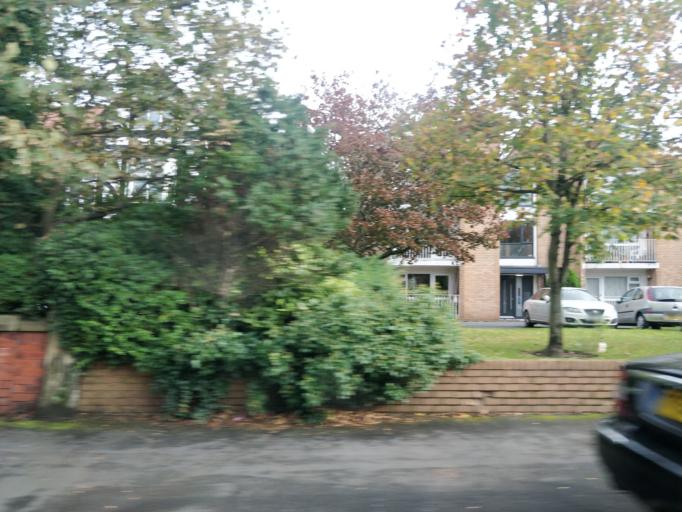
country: GB
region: England
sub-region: Sefton
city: Southport
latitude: 53.6585
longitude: -2.9806
